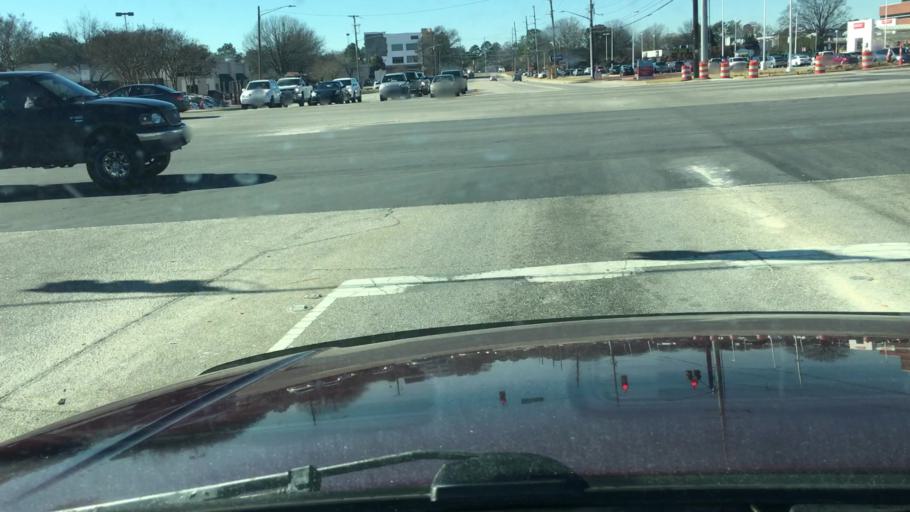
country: US
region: North Carolina
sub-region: Cumberland County
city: Fayetteville
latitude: 35.0308
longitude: -78.9301
